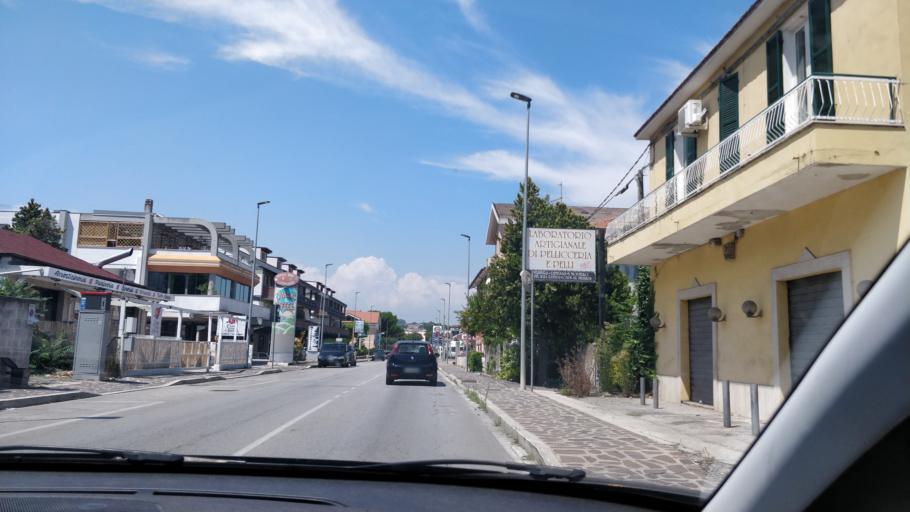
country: IT
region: Abruzzo
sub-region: Provincia di Chieti
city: Francavilla al Mare
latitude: 42.4219
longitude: 14.2844
